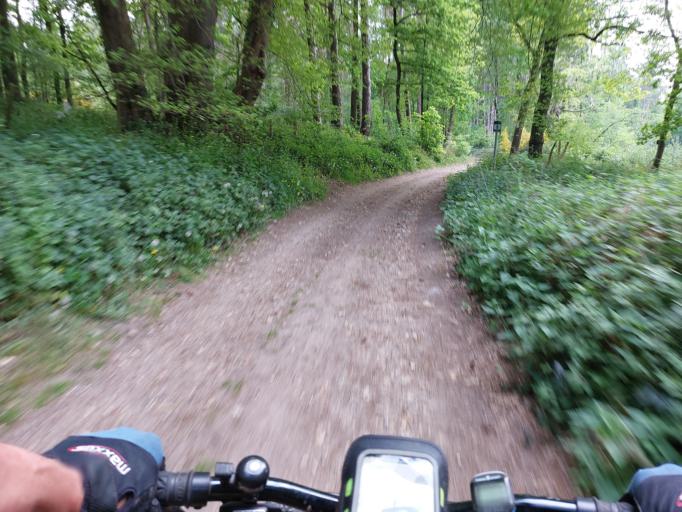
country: BE
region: Wallonia
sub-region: Province du Hainaut
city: Jurbise
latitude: 50.4954
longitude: 3.9020
